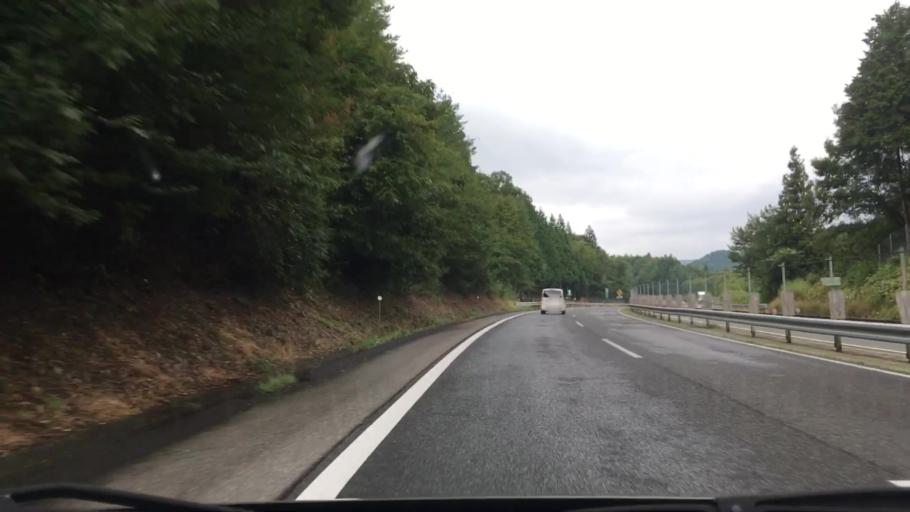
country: JP
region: Hiroshima
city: Miyoshi
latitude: 34.7189
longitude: 132.6492
